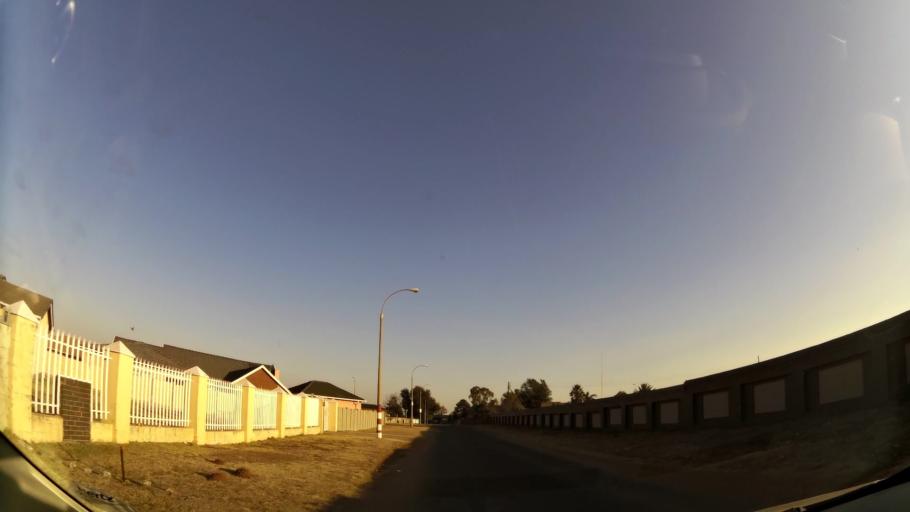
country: ZA
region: Gauteng
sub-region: West Rand District Municipality
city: Randfontein
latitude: -26.2067
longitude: 27.6479
